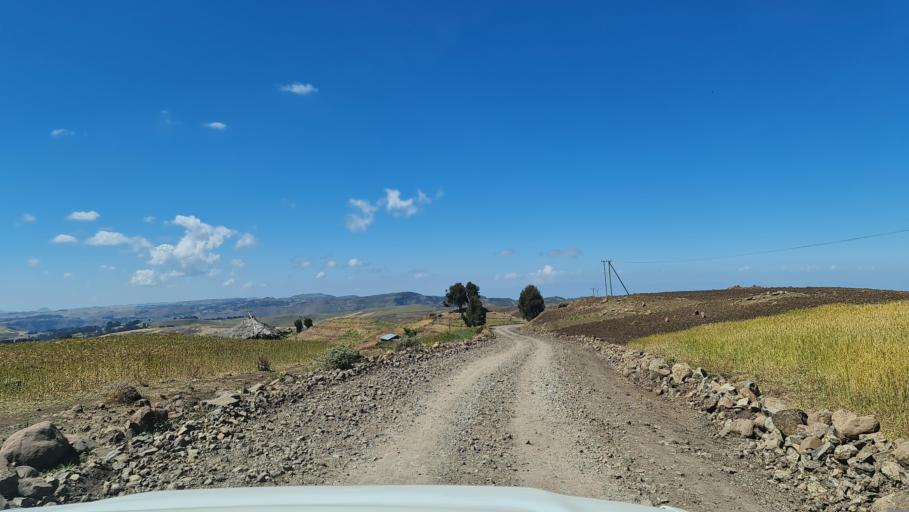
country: ET
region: Amhara
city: Debark'
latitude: 13.2291
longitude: 38.0941
